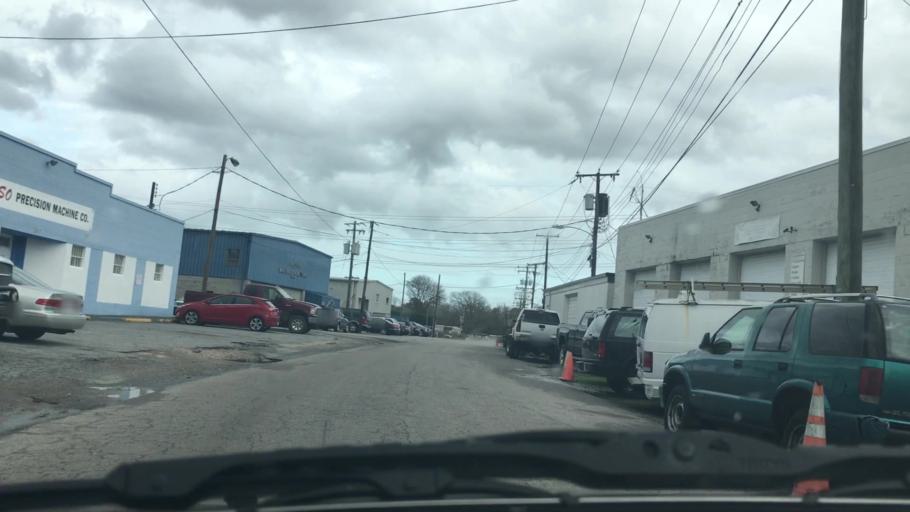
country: US
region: Virginia
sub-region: City of Norfolk
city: Norfolk
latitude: 36.8819
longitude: -76.2548
